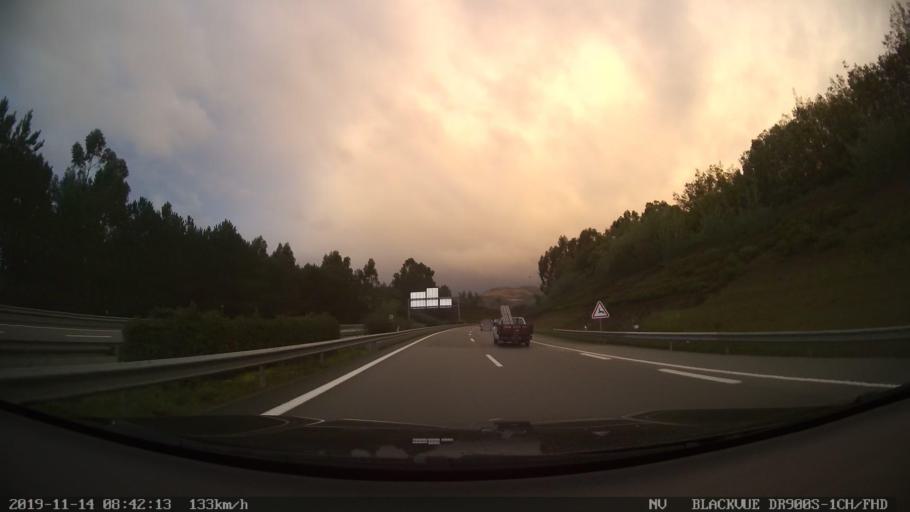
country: PT
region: Viana do Castelo
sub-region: Ponte de Lima
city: Ponte de Lima
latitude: 41.7808
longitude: -8.5669
